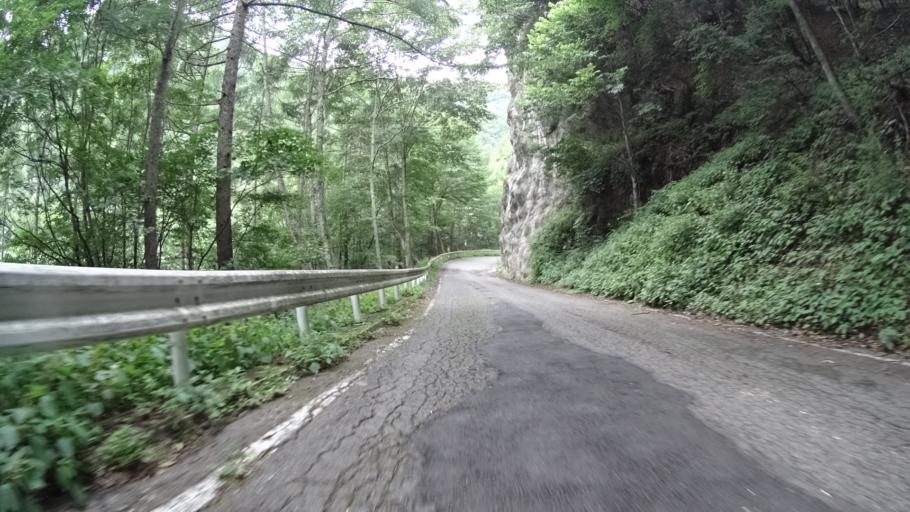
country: JP
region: Nagano
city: Saku
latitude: 36.0729
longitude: 138.6468
